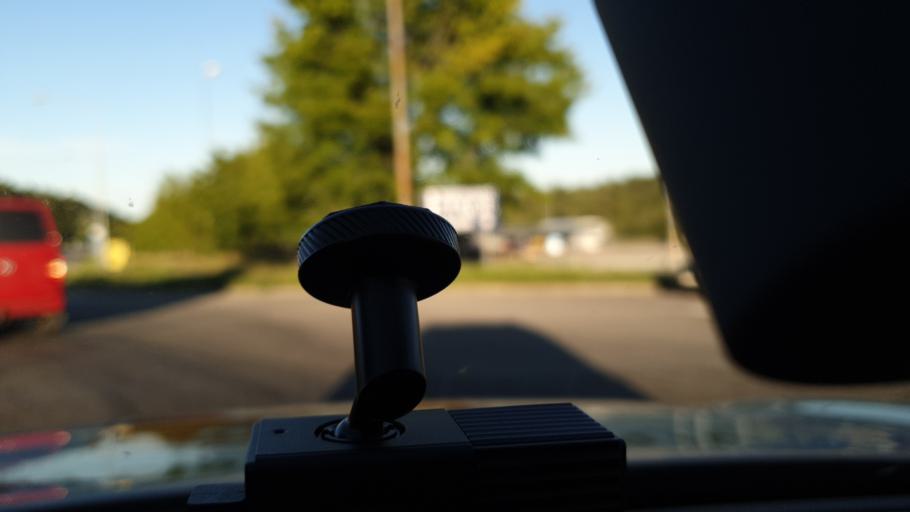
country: SE
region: Vaesternorrland
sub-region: Sundsvalls Kommun
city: Johannedal
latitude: 62.4131
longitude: 17.3496
